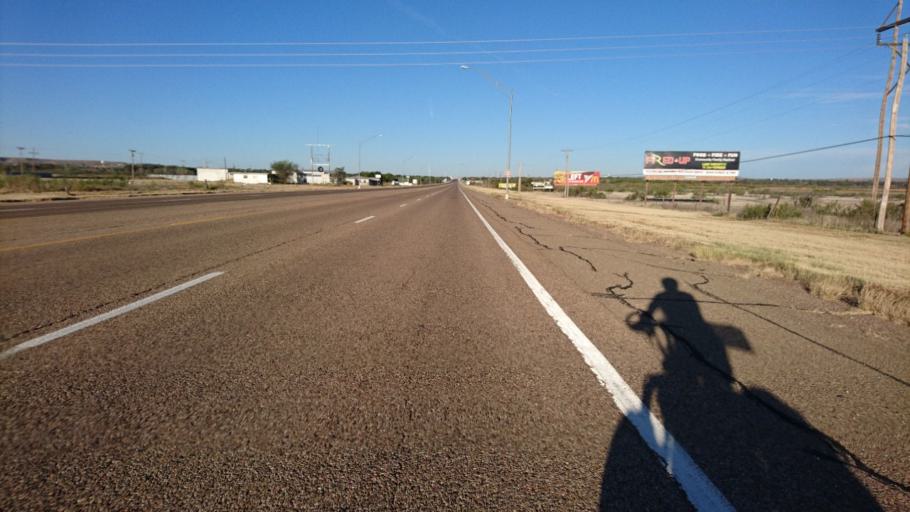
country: US
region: New Mexico
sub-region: Quay County
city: Tucumcari
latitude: 35.1720
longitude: -103.6882
